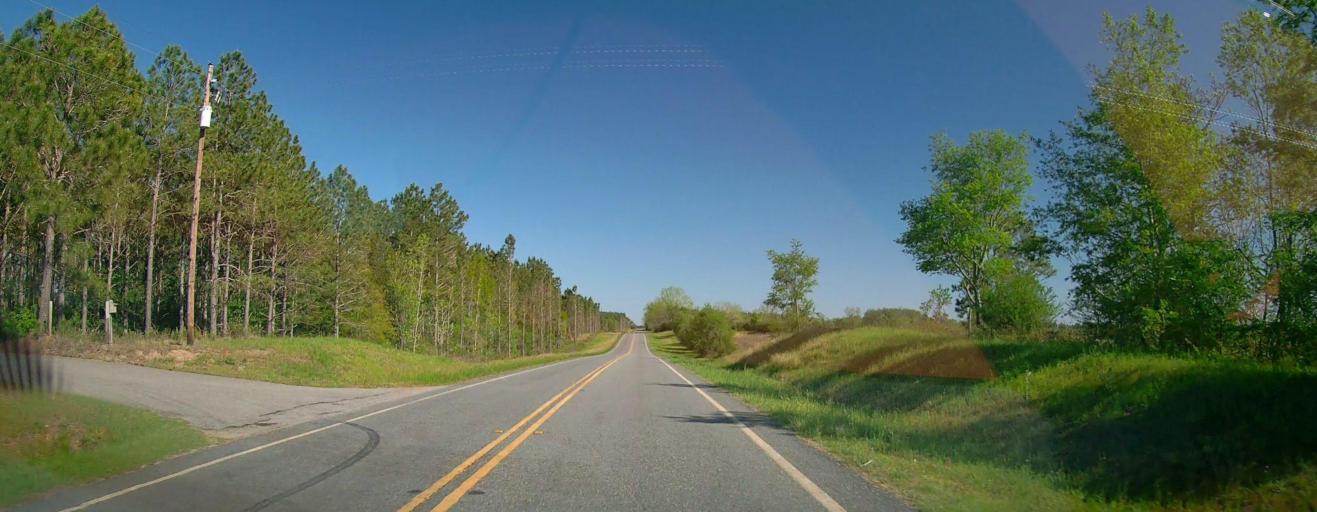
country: US
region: Georgia
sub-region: Wilcox County
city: Rochelle
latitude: 32.0016
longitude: -83.4808
